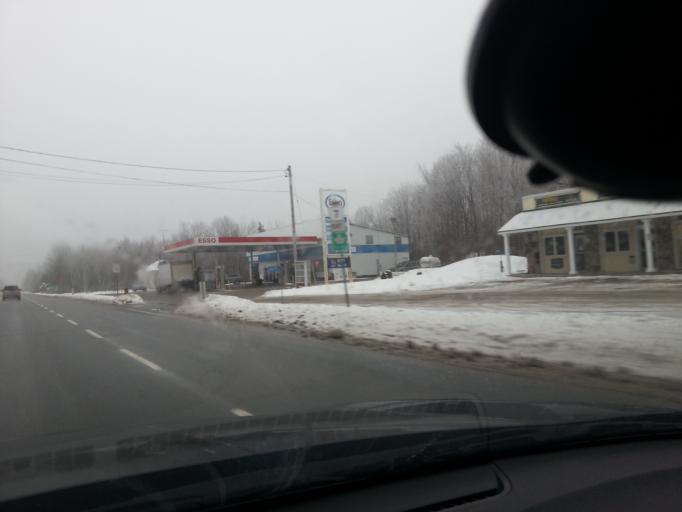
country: CA
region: Ontario
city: Perth
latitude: 44.7984
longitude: -76.6788
